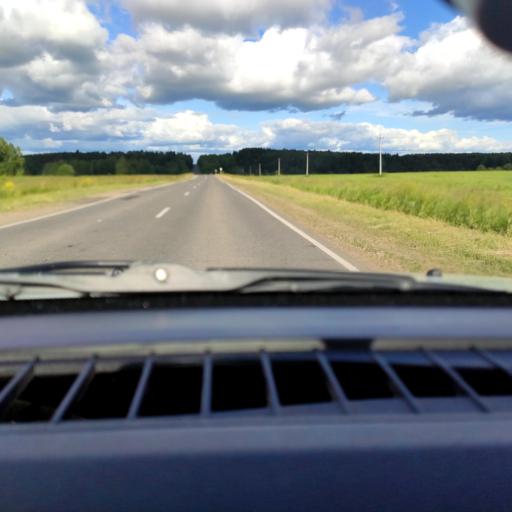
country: RU
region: Perm
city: Orda
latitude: 57.3290
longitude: 56.6886
